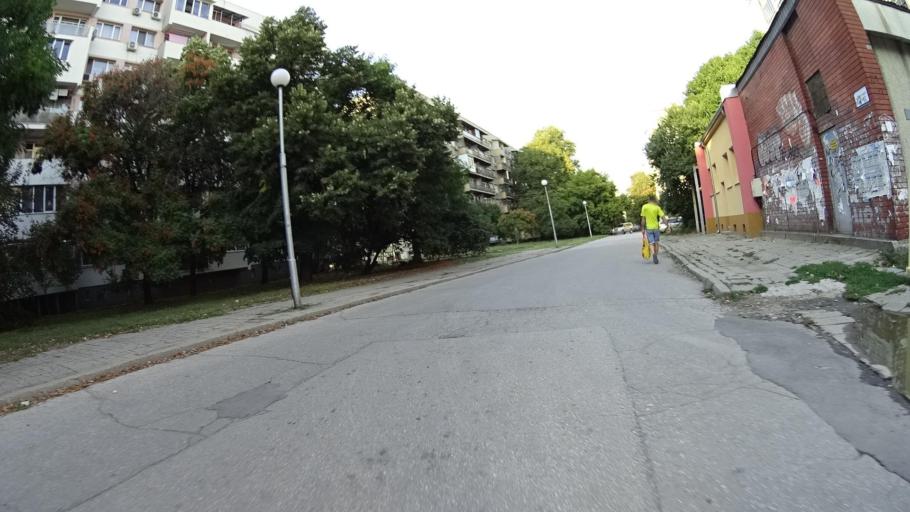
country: BG
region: Plovdiv
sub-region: Obshtina Plovdiv
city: Plovdiv
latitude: 42.1327
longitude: 24.7460
